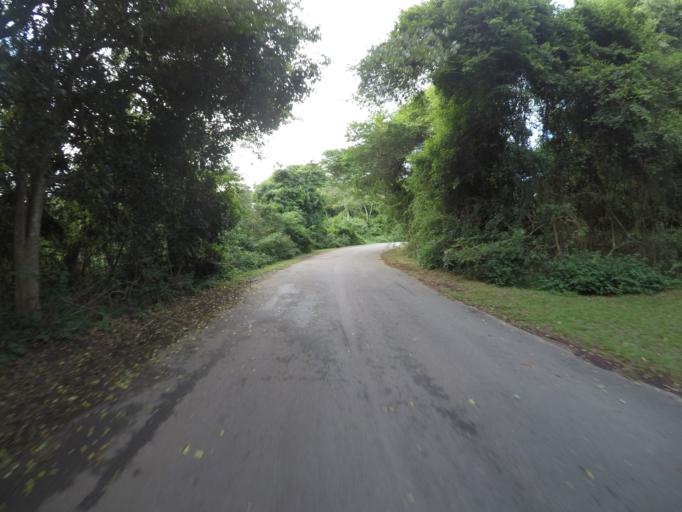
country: ZA
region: KwaZulu-Natal
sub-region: uMkhanyakude District Municipality
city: Mtubatuba
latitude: -28.3876
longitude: 32.4093
